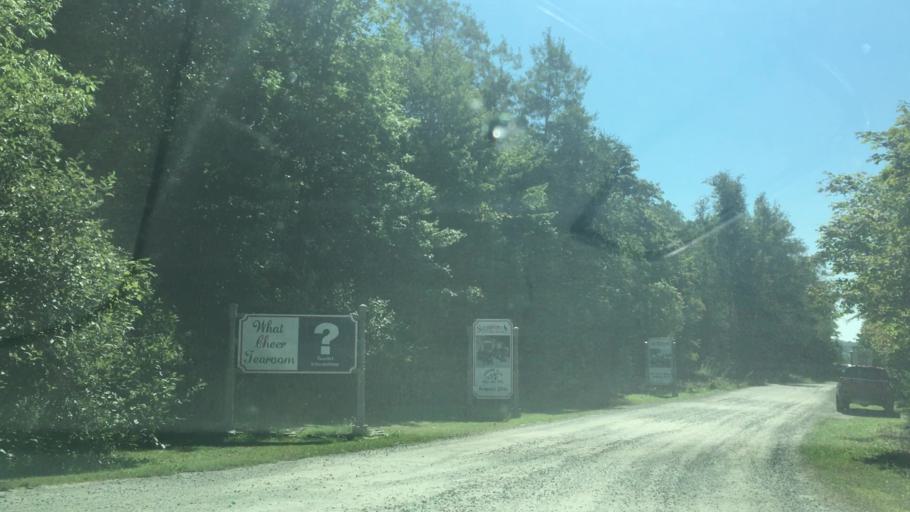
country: CA
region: Nova Scotia
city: Antigonish
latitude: 45.1406
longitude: -61.9829
